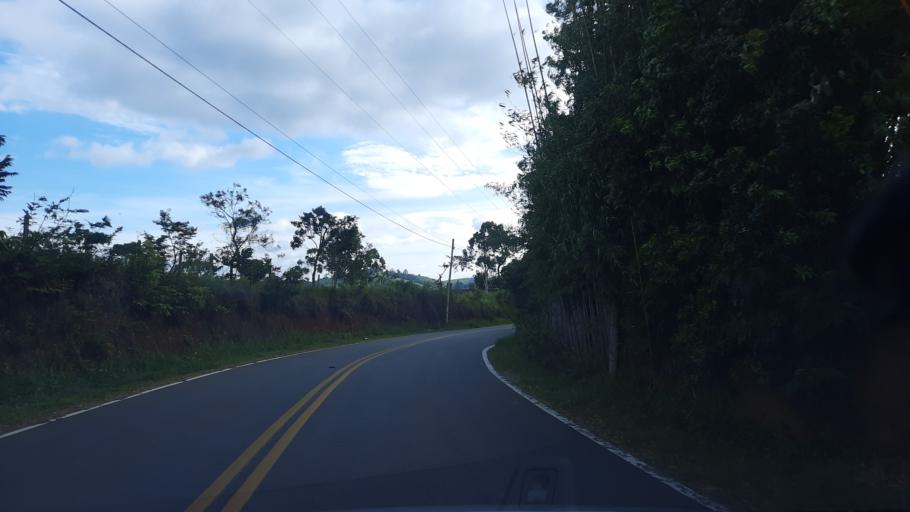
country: BR
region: Sao Paulo
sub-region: Atibaia
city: Atibaia
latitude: -23.0871
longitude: -46.5109
